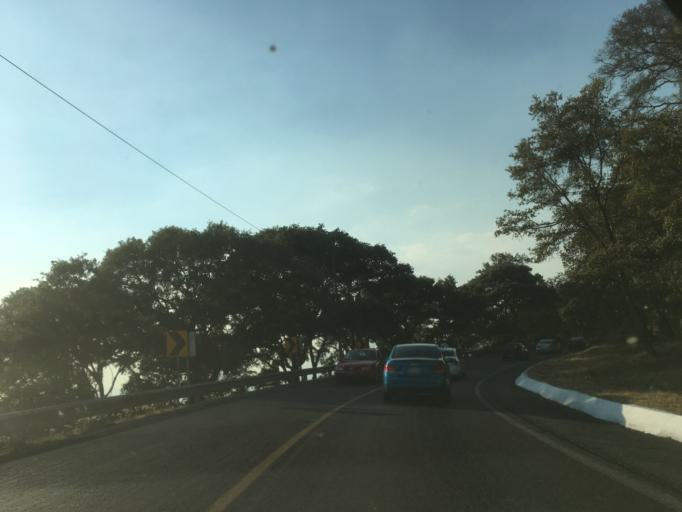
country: MX
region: Michoacan
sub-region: Morelia
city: Iratzio
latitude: 19.6244
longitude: -101.4599
